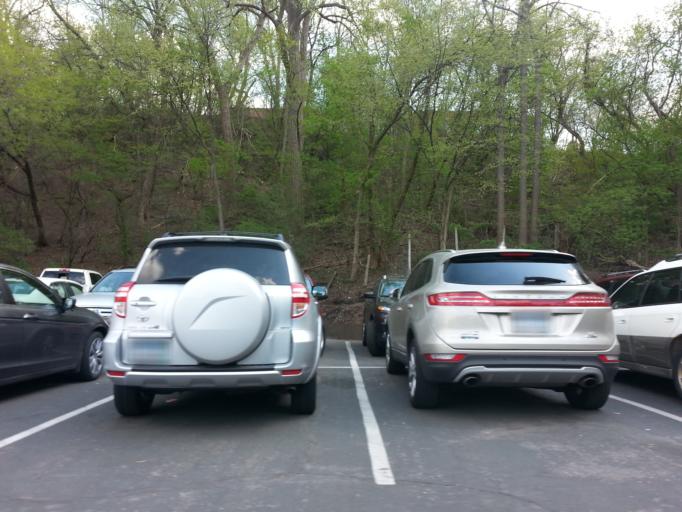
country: US
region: Minnesota
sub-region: Washington County
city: Stillwater
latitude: 45.0484
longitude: -92.8050
